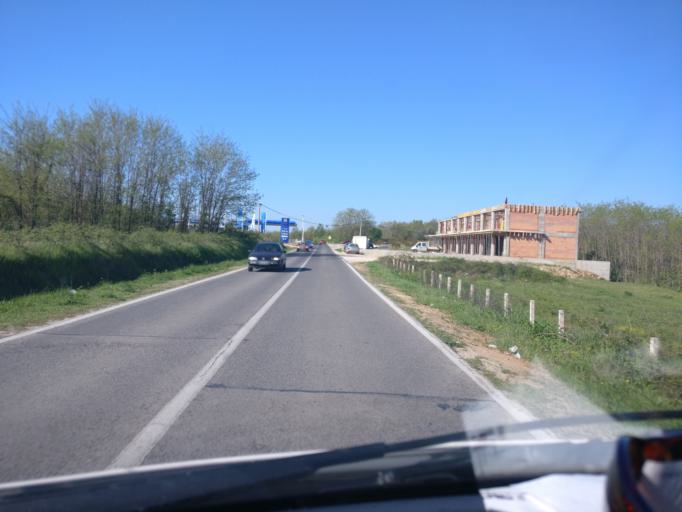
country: BA
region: Federation of Bosnia and Herzegovina
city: Tasovcici
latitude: 43.1351
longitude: 17.7751
